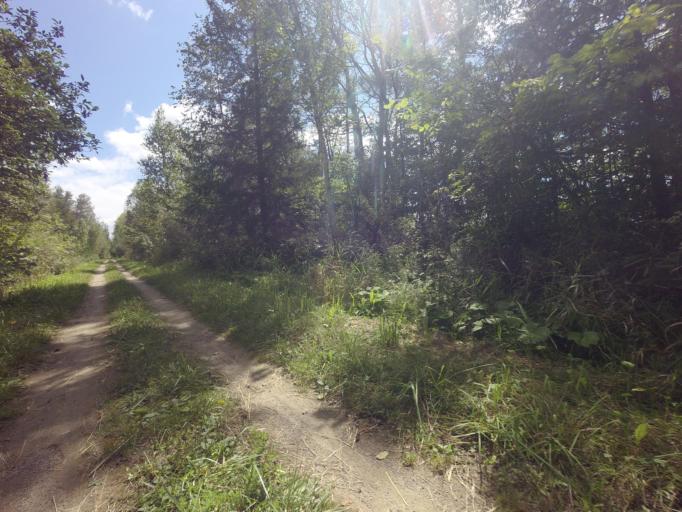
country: CA
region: Ontario
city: Orangeville
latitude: 43.7935
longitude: -80.2714
